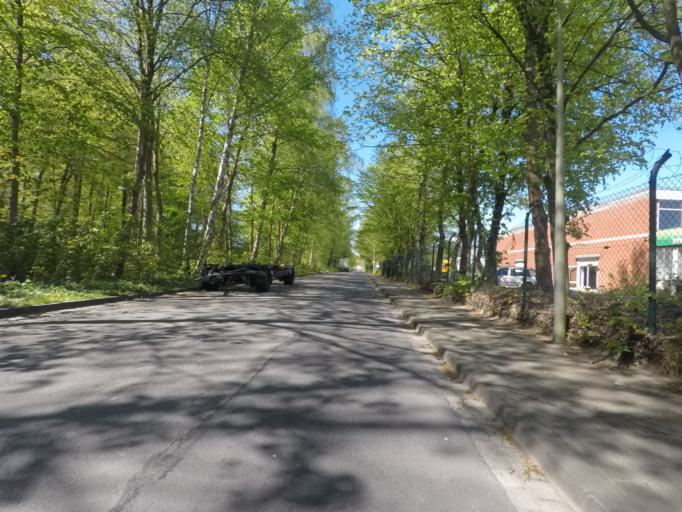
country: DE
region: North Rhine-Westphalia
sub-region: Regierungsbezirk Detmold
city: Bielefeld
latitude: 52.0111
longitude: 8.5795
